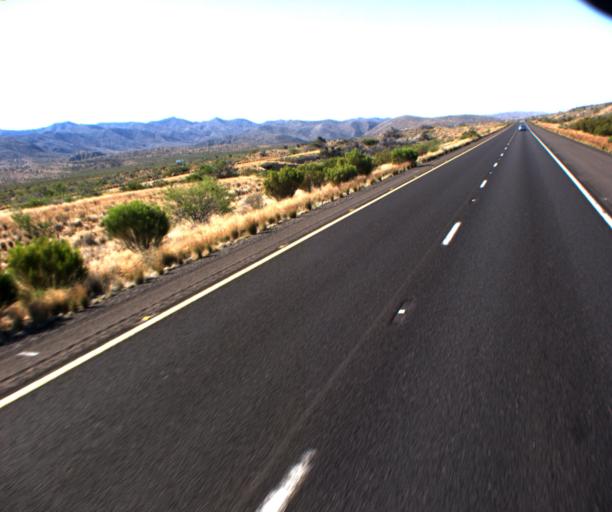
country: US
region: Arizona
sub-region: Mohave County
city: Kingman
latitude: 35.0543
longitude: -113.6655
